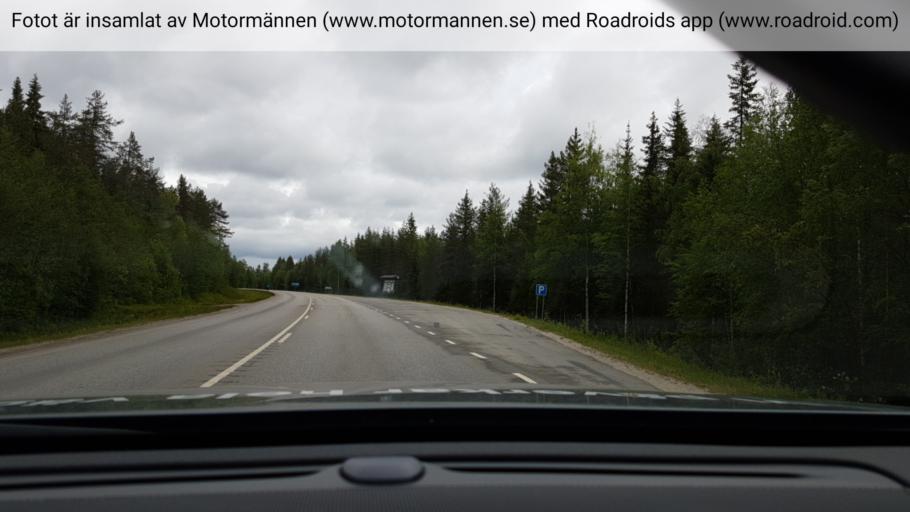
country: SE
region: Vaesterbotten
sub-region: Lycksele Kommun
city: Lycksele
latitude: 64.5791
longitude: 18.6571
